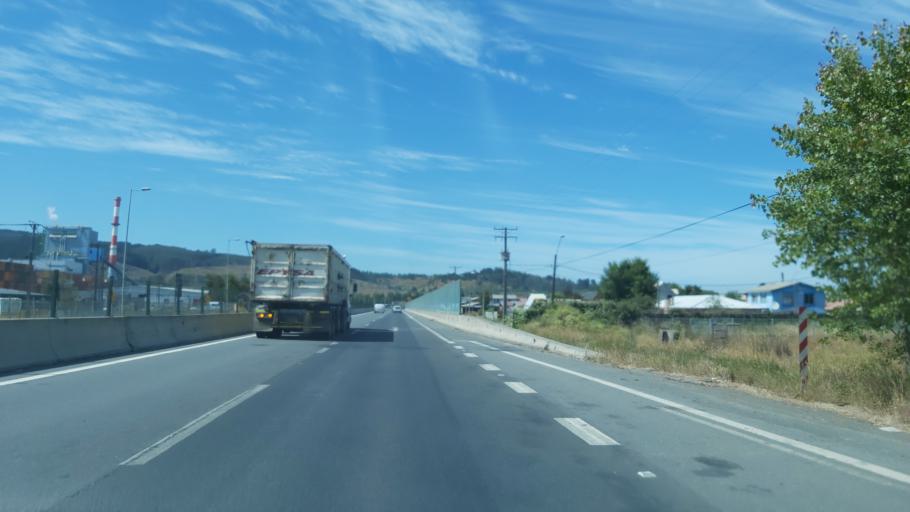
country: CL
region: Biobio
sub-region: Provincia de Concepcion
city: Coronel
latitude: -37.0348
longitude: -73.1349
